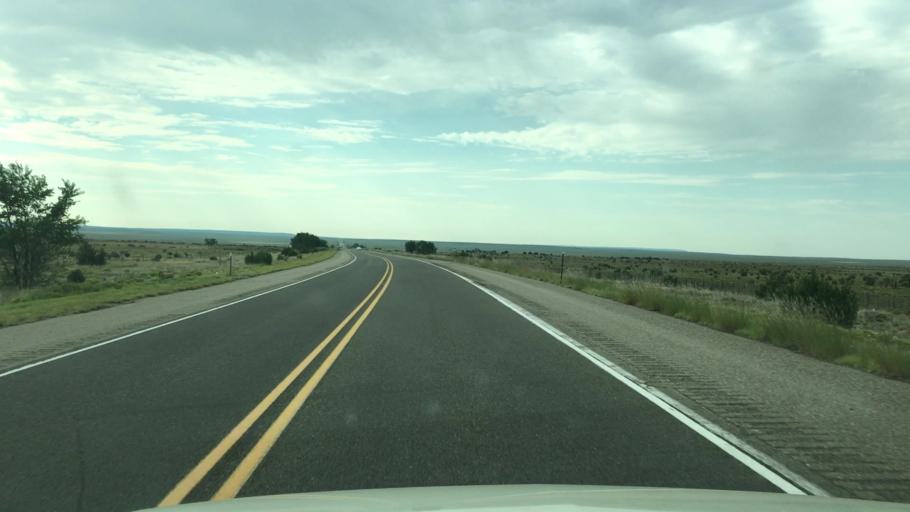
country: US
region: New Mexico
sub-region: Santa Fe County
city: Eldorado at Santa Fe
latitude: 35.2194
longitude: -105.7998
